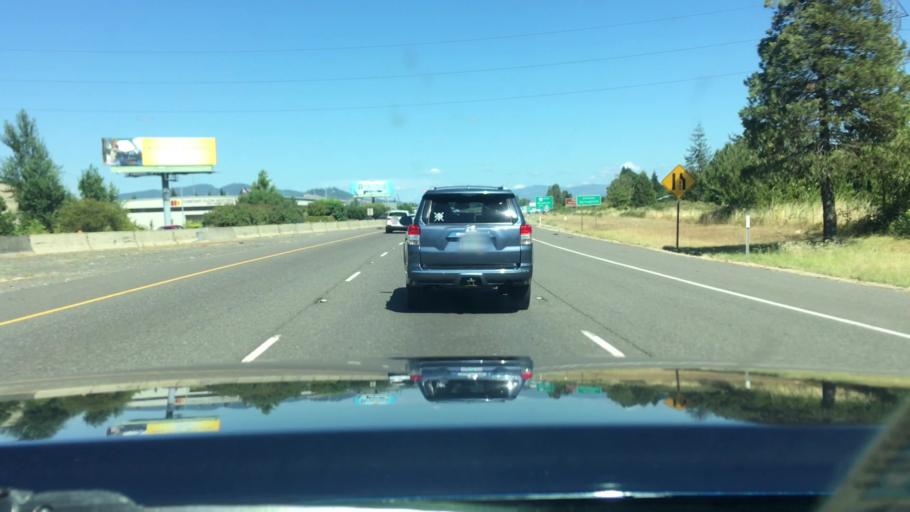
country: US
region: Oregon
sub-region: Lane County
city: Springfield
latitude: 44.0630
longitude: -123.0423
